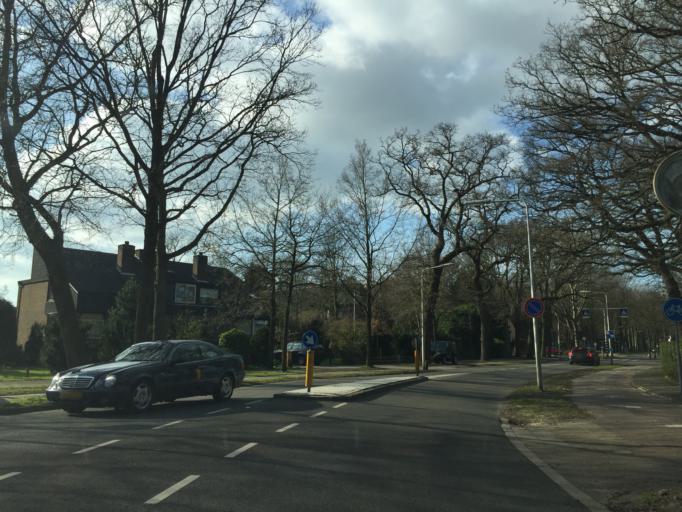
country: NL
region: South Holland
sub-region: Gemeente Wassenaar
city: Wassenaar
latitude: 52.1174
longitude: 4.3691
